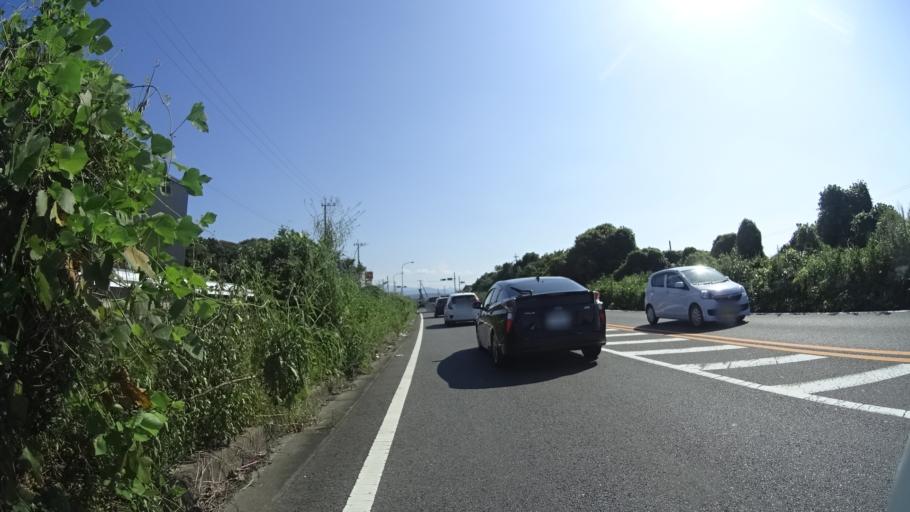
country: JP
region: Fukuoka
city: Yukuhashi
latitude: 33.6983
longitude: 130.9953
